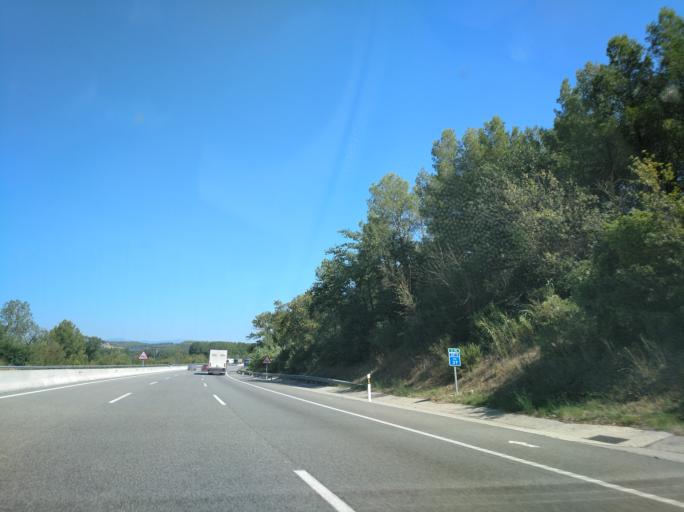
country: ES
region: Catalonia
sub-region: Provincia de Girona
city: Bascara
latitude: 42.1579
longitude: 2.9170
